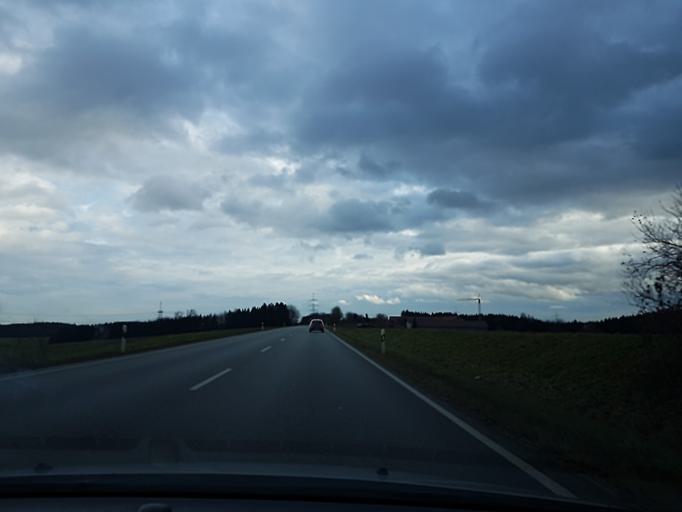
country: DE
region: Bavaria
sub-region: Lower Bavaria
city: Geisenhausen
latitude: 48.4987
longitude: 12.2206
